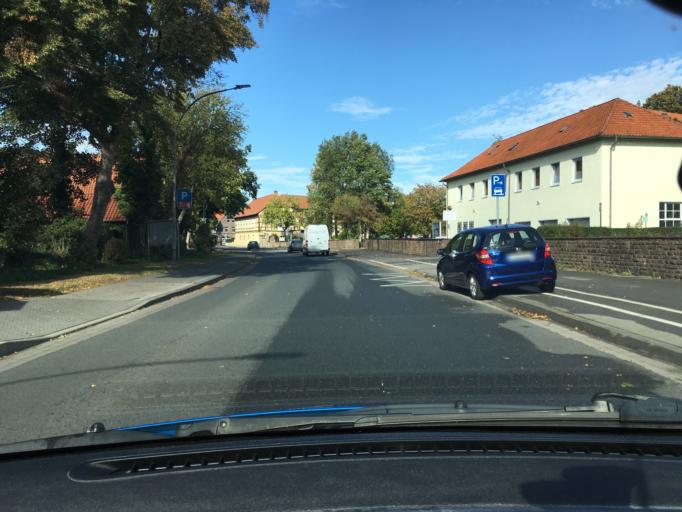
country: DE
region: Lower Saxony
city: Springe
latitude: 52.2059
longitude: 9.5557
